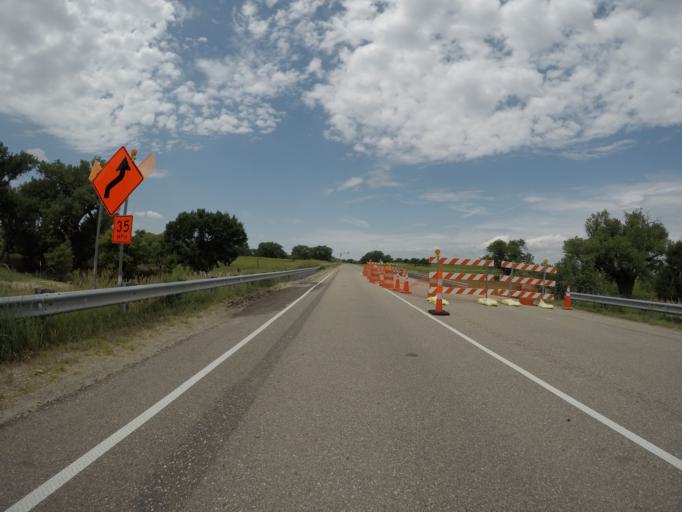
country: US
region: Kansas
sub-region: Graham County
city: Hill City
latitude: 39.3943
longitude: -99.6344
